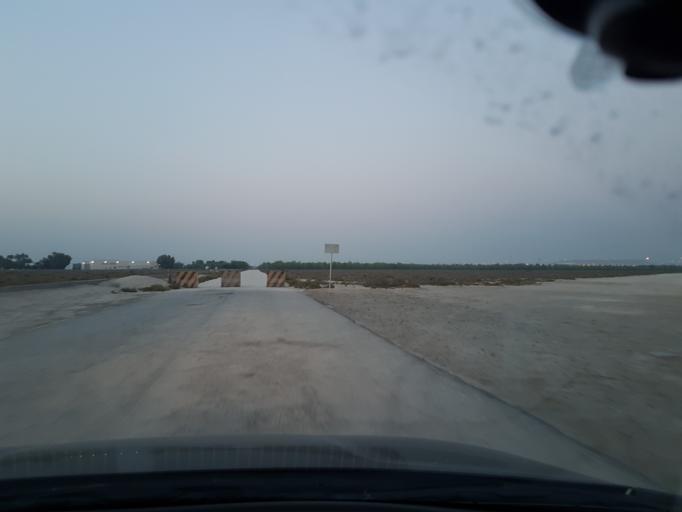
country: BH
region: Central Governorate
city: Dar Kulayb
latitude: 26.0092
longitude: 50.4756
